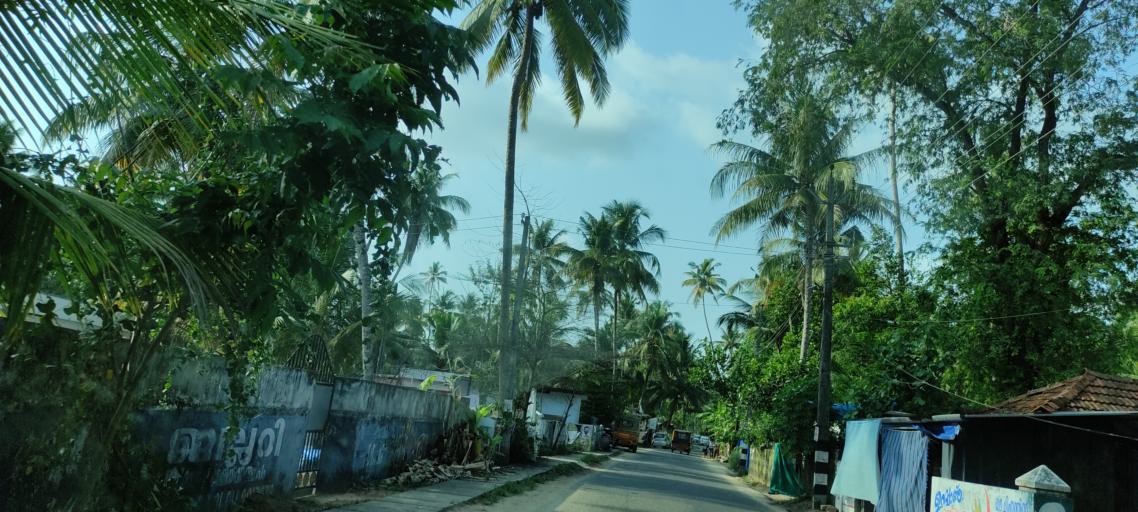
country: IN
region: Kerala
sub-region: Alappuzha
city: Vayalar
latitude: 9.7054
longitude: 76.2891
